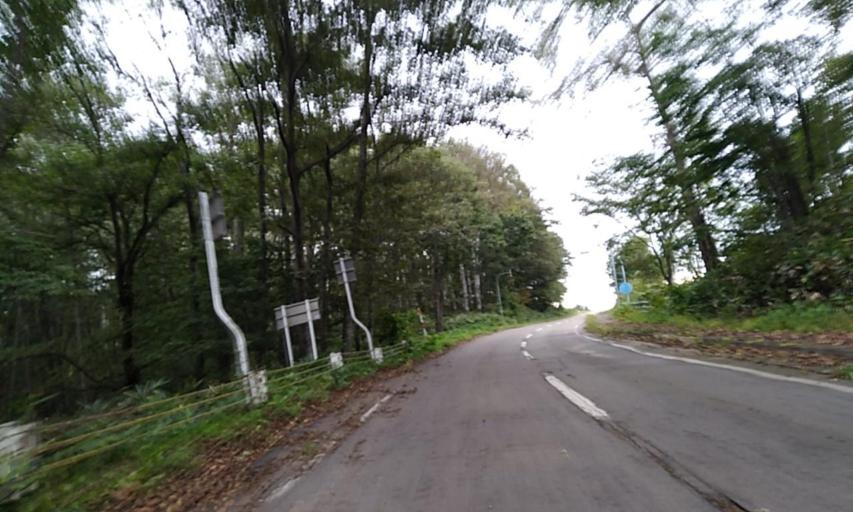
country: JP
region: Hokkaido
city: Obihiro
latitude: 42.6728
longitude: 143.0496
